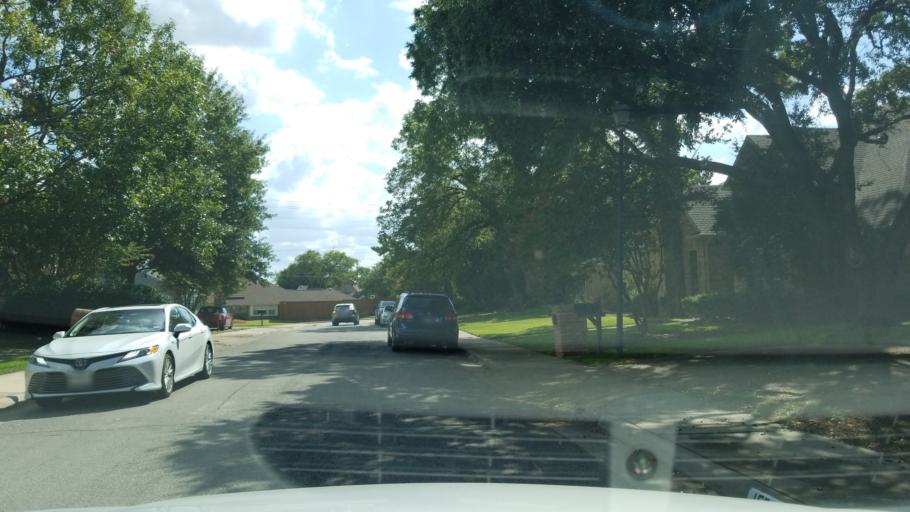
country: US
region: Texas
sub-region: Dallas County
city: Addison
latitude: 32.9605
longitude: -96.7971
